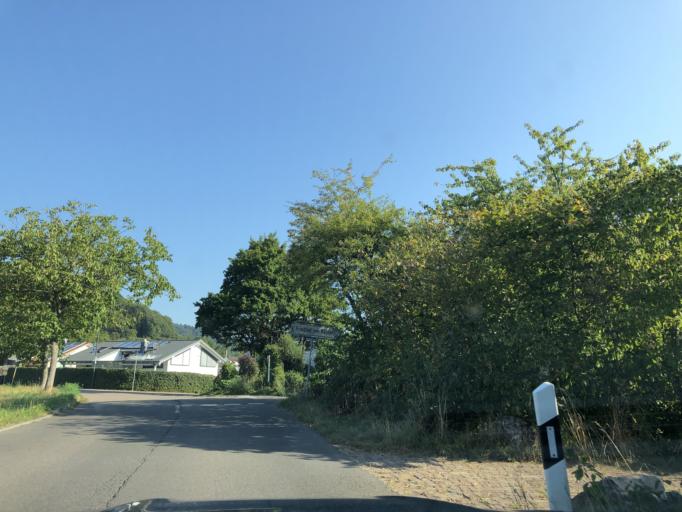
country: DE
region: Baden-Wuerttemberg
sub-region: Karlsruhe Region
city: Wilhelmsfeld
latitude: 49.4217
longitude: 8.7452
